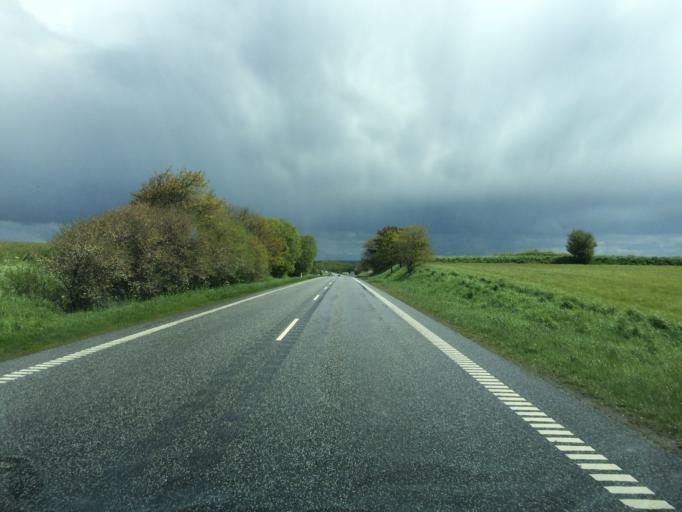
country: DK
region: Central Jutland
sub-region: Skive Kommune
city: Hojslev
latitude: 56.5897
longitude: 9.2109
